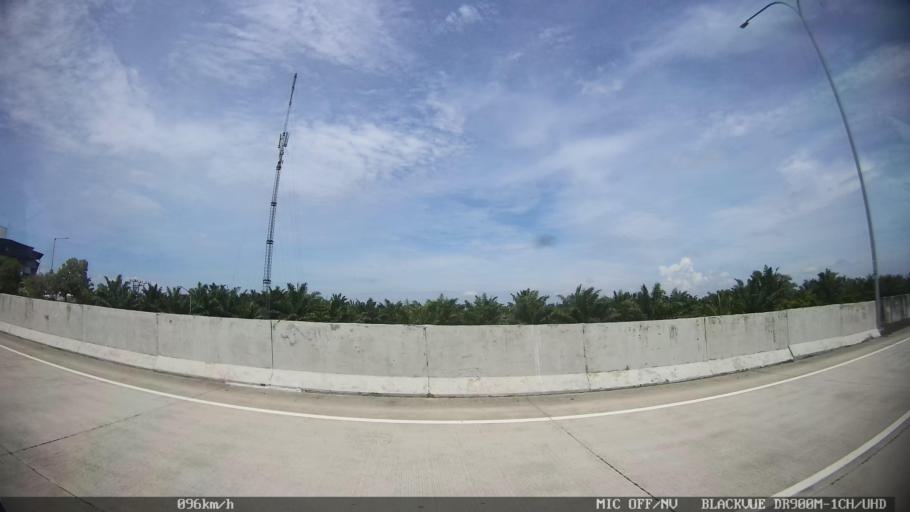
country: ID
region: North Sumatra
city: Percut
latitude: 3.5906
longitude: 98.8446
